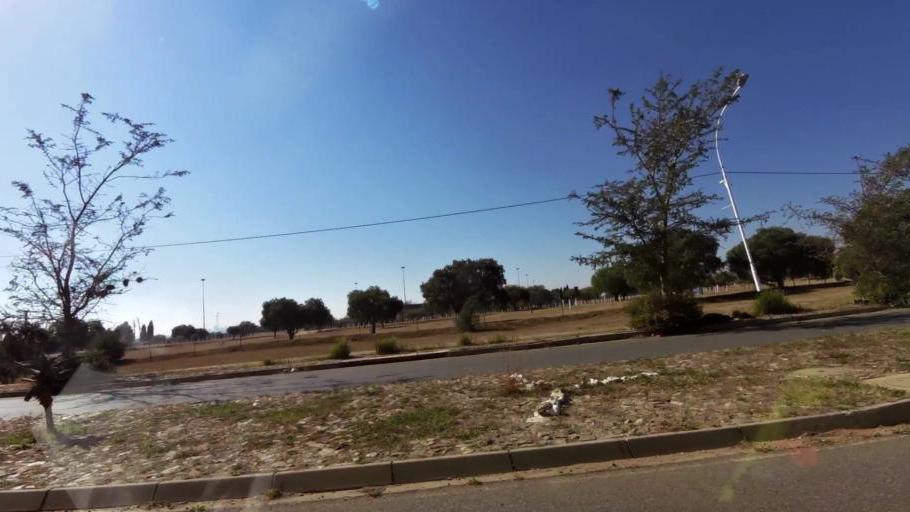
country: ZA
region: Gauteng
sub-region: City of Johannesburg Metropolitan Municipality
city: Johannesburg
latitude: -26.2467
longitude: 27.9753
